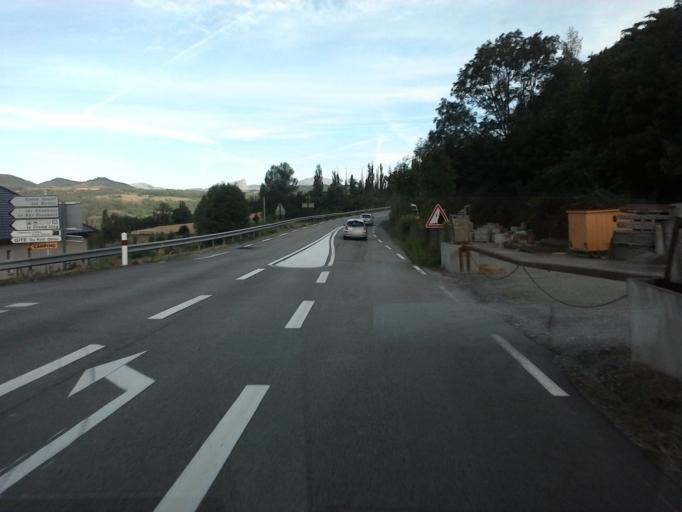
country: FR
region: Rhone-Alpes
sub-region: Departement de l'Isere
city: La Mure
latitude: 44.8637
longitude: 5.8566
